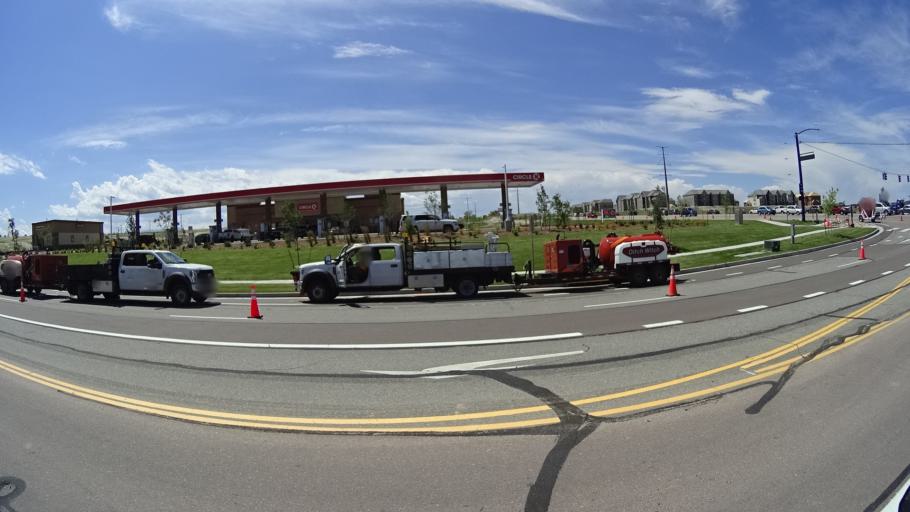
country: US
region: Colorado
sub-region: El Paso County
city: Black Forest
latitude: 38.9404
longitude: -104.7010
